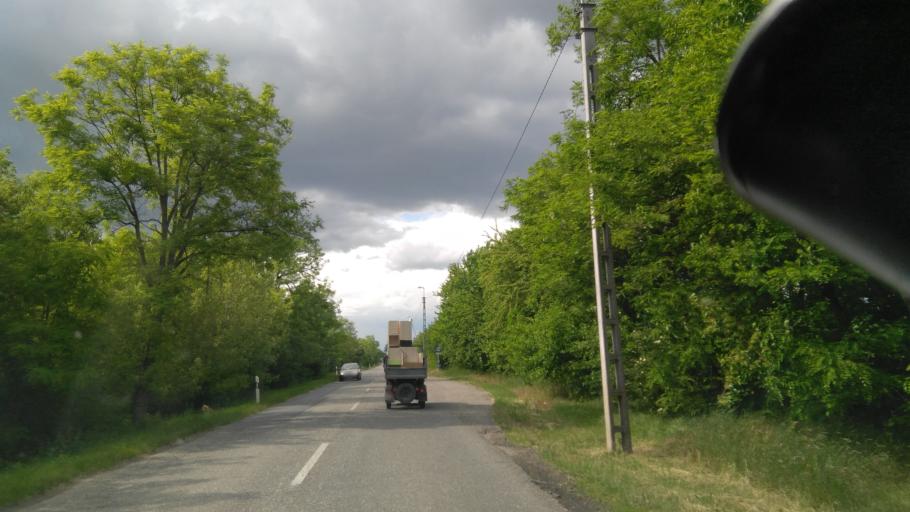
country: HU
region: Bekes
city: Oroshaza
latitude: 46.5816
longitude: 20.6474
